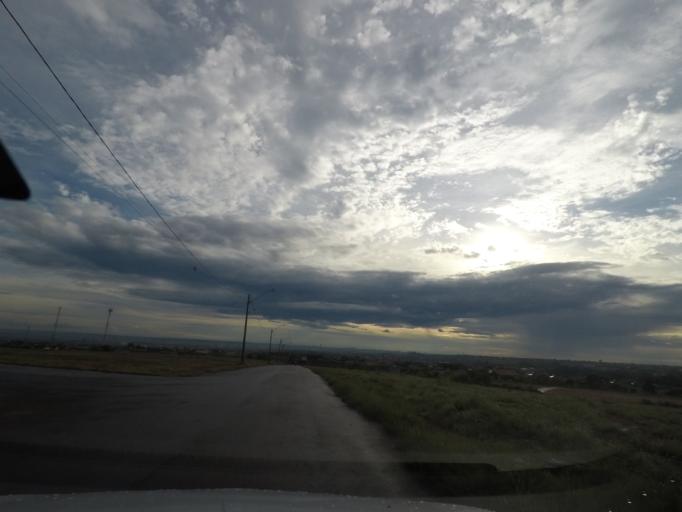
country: BR
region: Goias
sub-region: Goiania
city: Goiania
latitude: -16.7554
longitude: -49.3786
